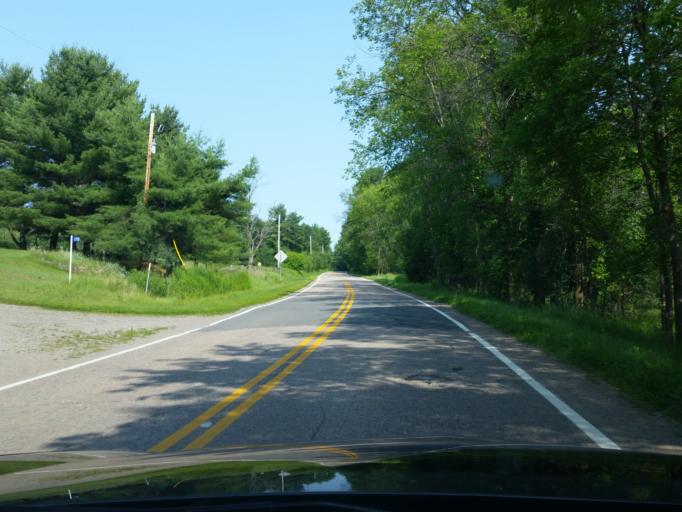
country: CA
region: Quebec
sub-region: Outaouais
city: Shawville
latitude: 45.5234
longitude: -76.4458
